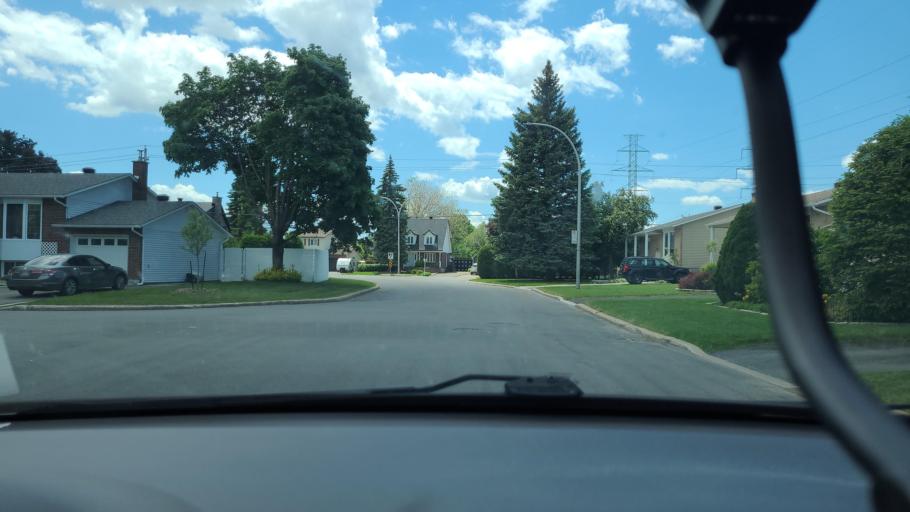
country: CA
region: Quebec
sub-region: Laval
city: Laval
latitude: 45.6120
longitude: -73.7289
